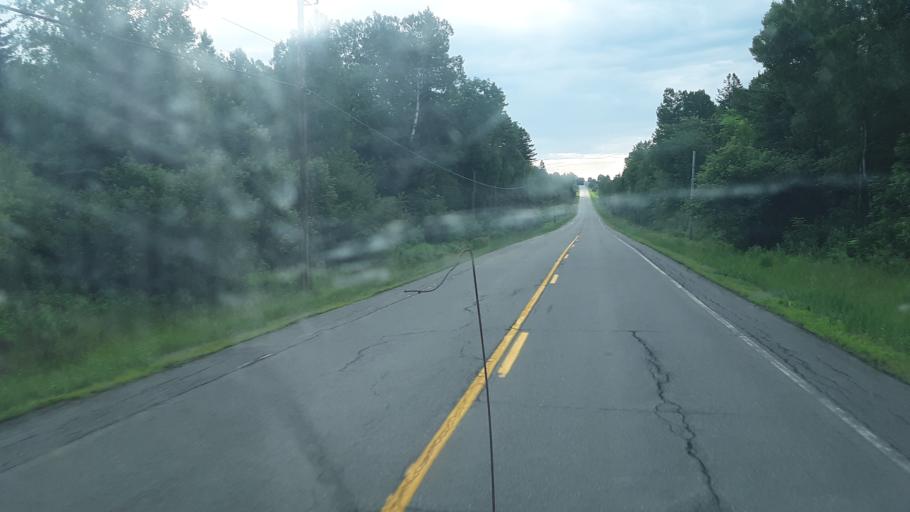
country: US
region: Maine
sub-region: Penobscot County
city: Patten
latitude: 45.8709
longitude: -68.3449
